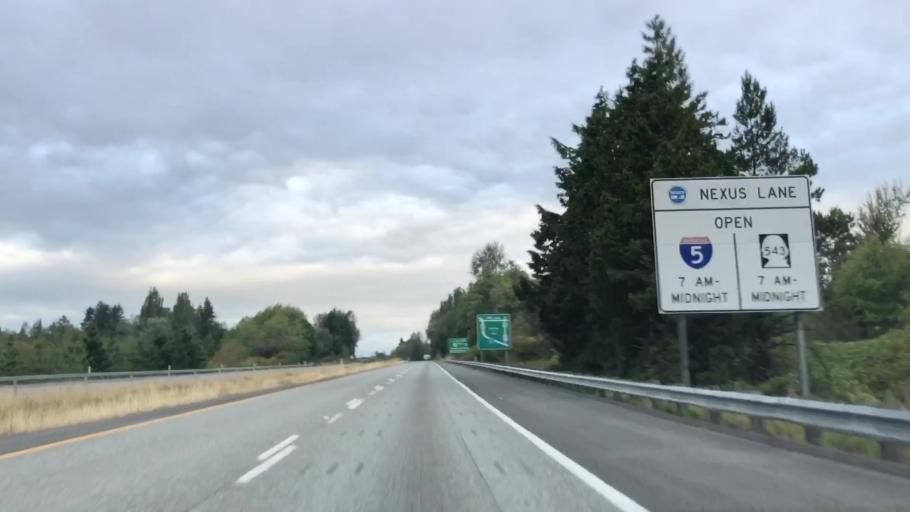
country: US
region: Washington
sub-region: Whatcom County
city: Blaine
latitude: 48.9816
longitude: -122.7307
